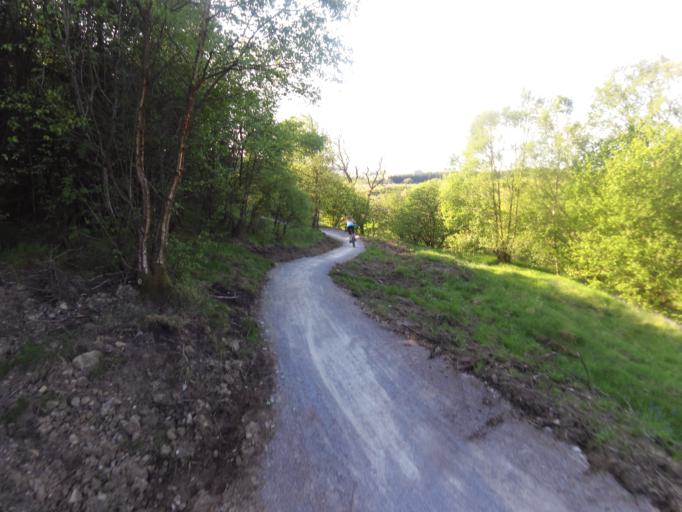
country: GB
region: England
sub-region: North Yorkshire
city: Settle
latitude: 54.0065
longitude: -2.3841
